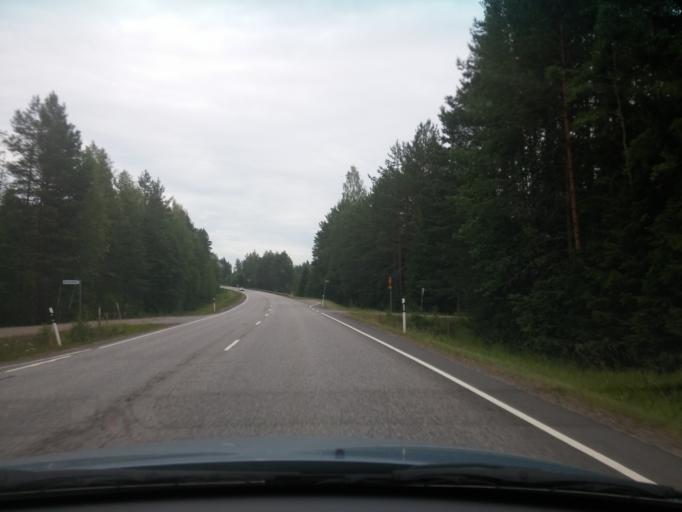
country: FI
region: Haeme
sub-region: Riihimaeki
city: Loppi
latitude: 60.7273
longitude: 24.4052
